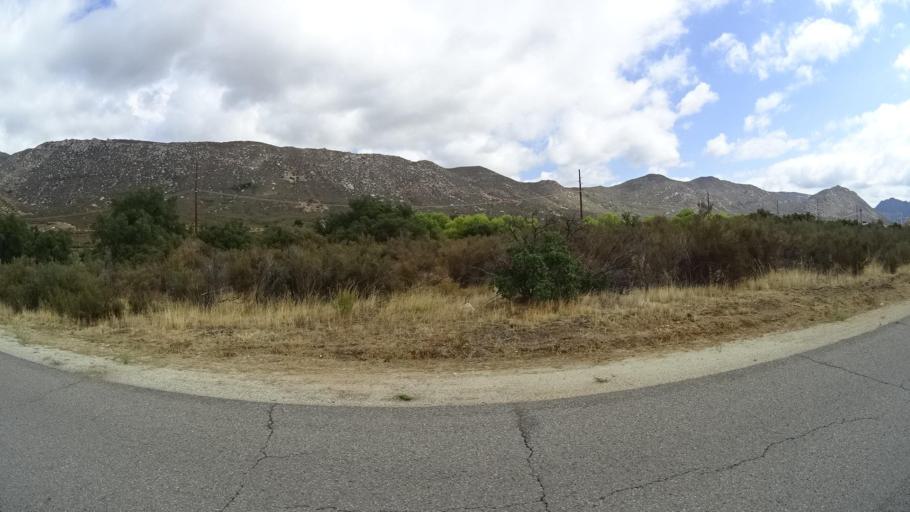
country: US
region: California
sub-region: San Diego County
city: Pine Valley
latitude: 32.7671
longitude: -116.4926
